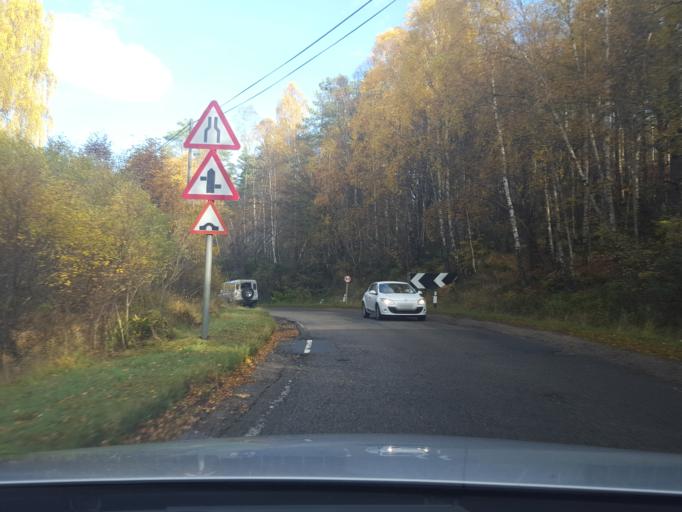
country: GB
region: Scotland
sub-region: Highland
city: Spean Bridge
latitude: 57.1746
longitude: -4.7984
